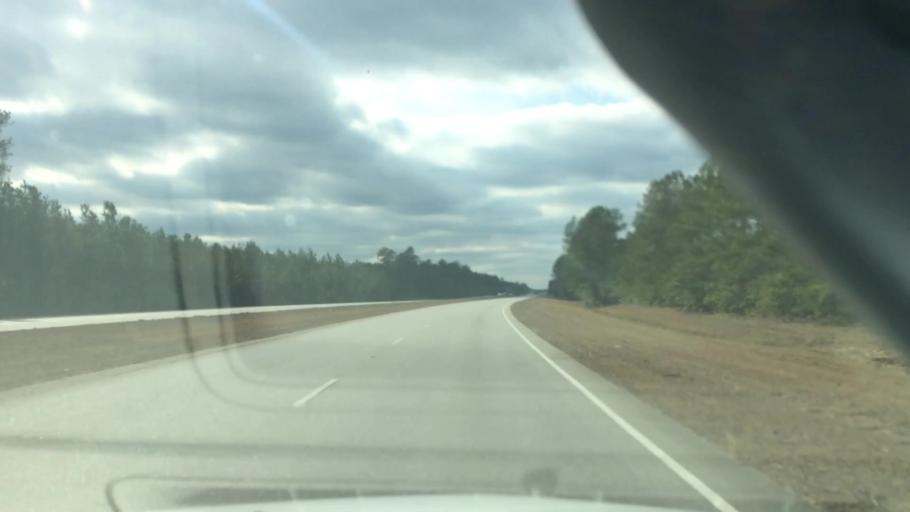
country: US
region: North Carolina
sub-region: Brunswick County
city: Bolivia
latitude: 34.0503
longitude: -78.2201
